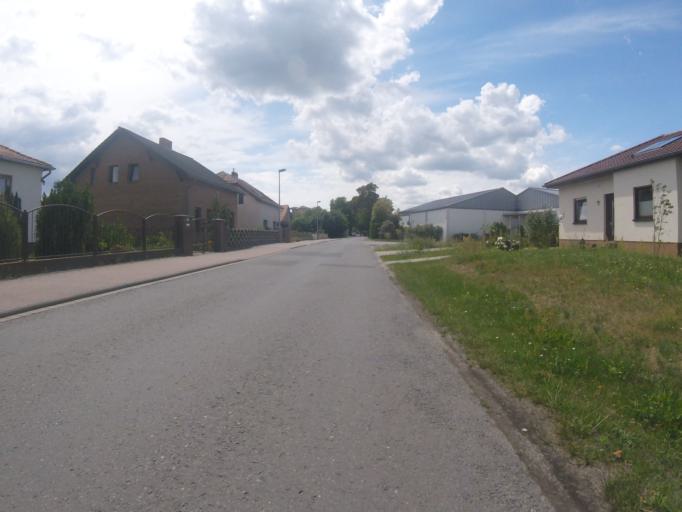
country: DE
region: Brandenburg
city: Bestensee
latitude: 52.2443
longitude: 13.6370
